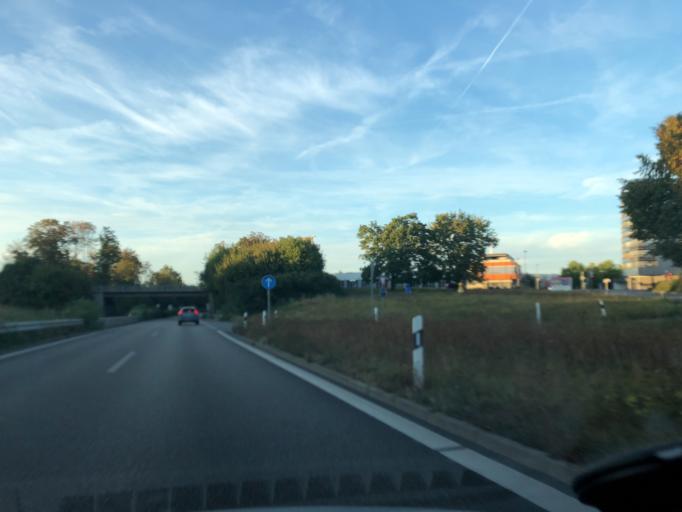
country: DE
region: Baden-Wuerttemberg
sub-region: Regierungsbezirk Stuttgart
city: Kornwestheim
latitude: 48.8592
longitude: 9.1962
